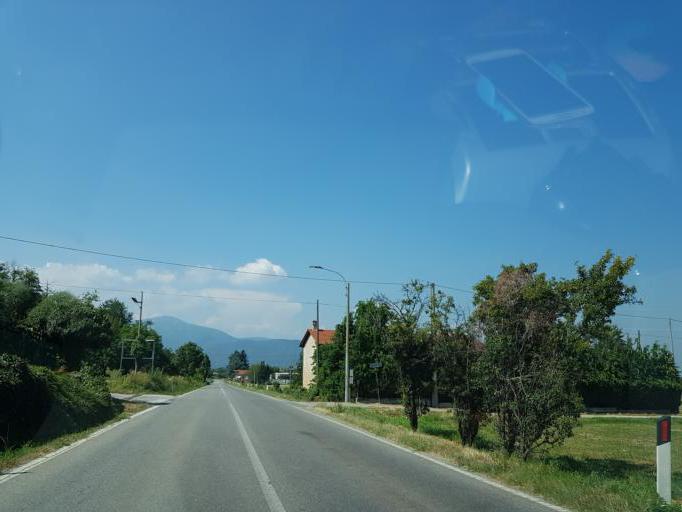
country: IT
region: Piedmont
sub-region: Provincia di Cuneo
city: Caraglio
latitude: 44.4285
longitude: 7.4254
